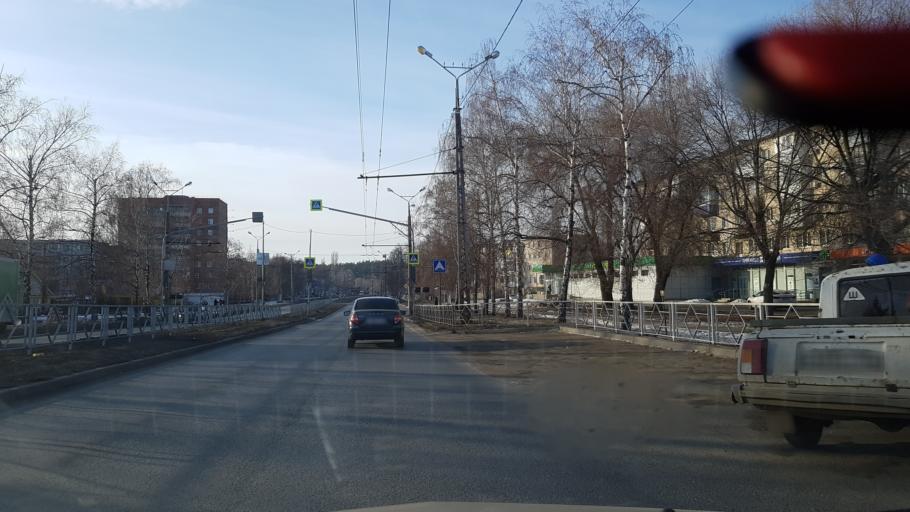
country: RU
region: Samara
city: Tol'yatti
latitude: 53.5299
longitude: 49.4049
